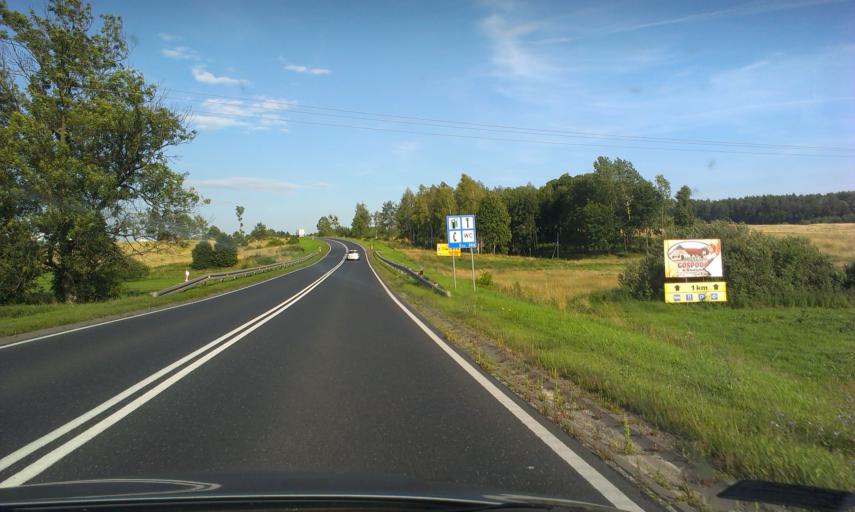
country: PL
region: Kujawsko-Pomorskie
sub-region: Powiat bydgoski
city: Sicienko
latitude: 53.1605
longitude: 17.8190
